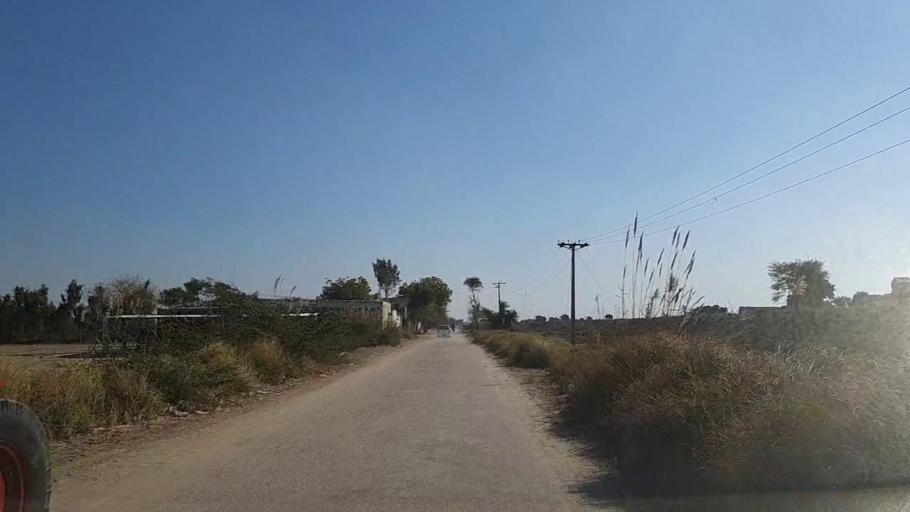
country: PK
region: Sindh
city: Nawabshah
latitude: 26.2397
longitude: 68.4241
